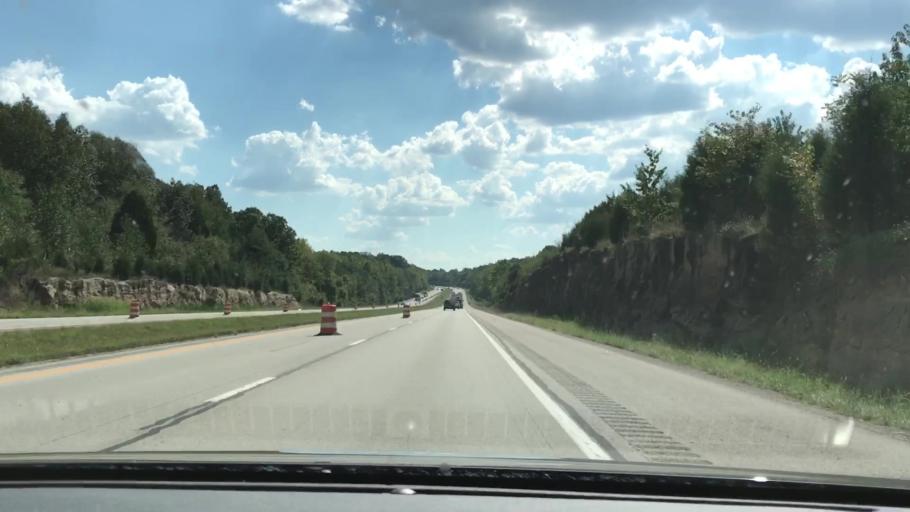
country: US
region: Kentucky
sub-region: Ohio County
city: Oak Grove
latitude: 37.2759
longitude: -86.7457
